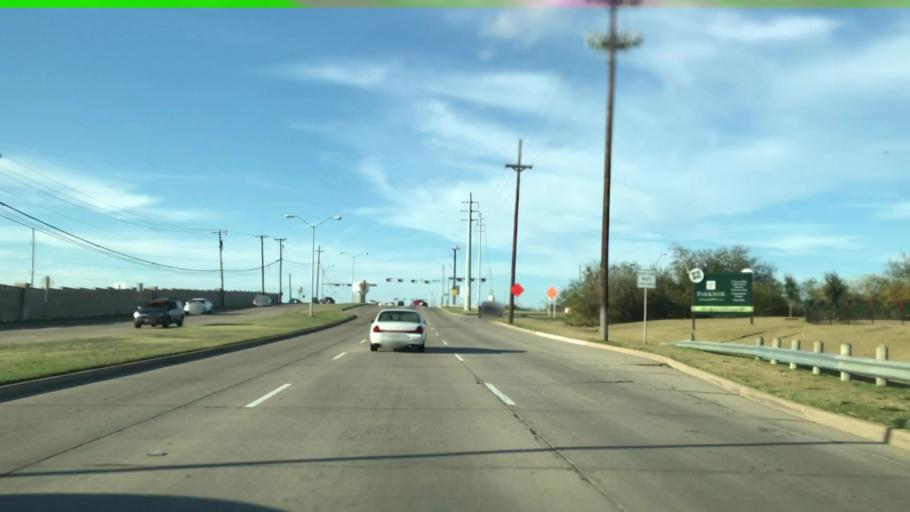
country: US
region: Texas
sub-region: Dallas County
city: Coppell
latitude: 32.9032
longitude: -96.9915
